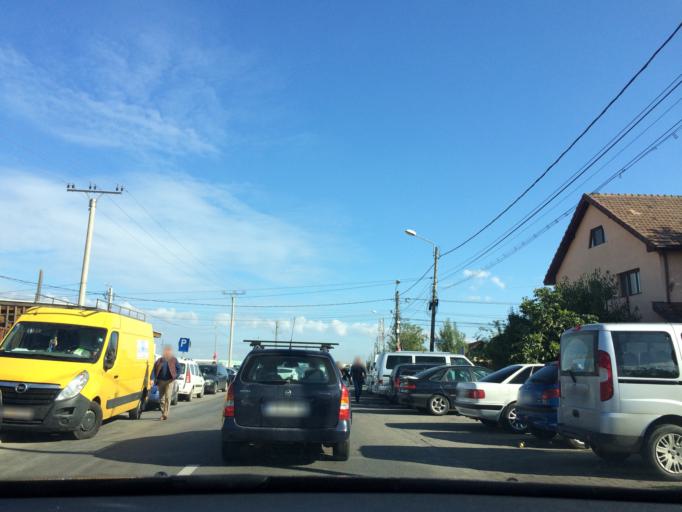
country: RO
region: Timis
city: Timisoara
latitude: 45.7696
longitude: 21.1962
